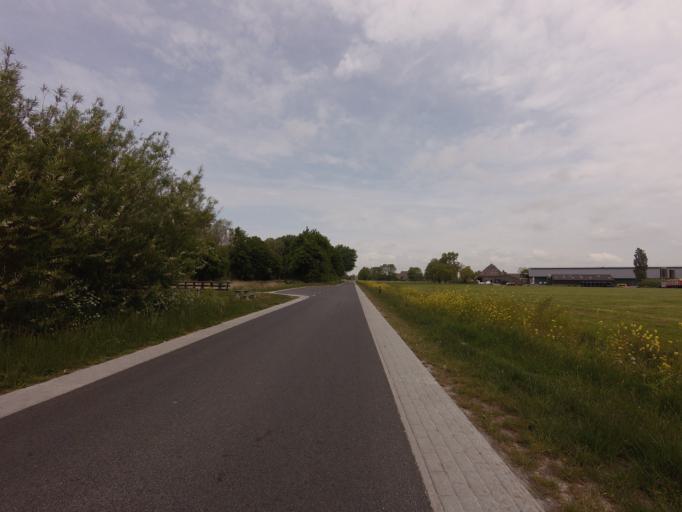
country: NL
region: Friesland
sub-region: Sudwest Fryslan
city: Bolsward
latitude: 53.0948
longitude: 5.4776
